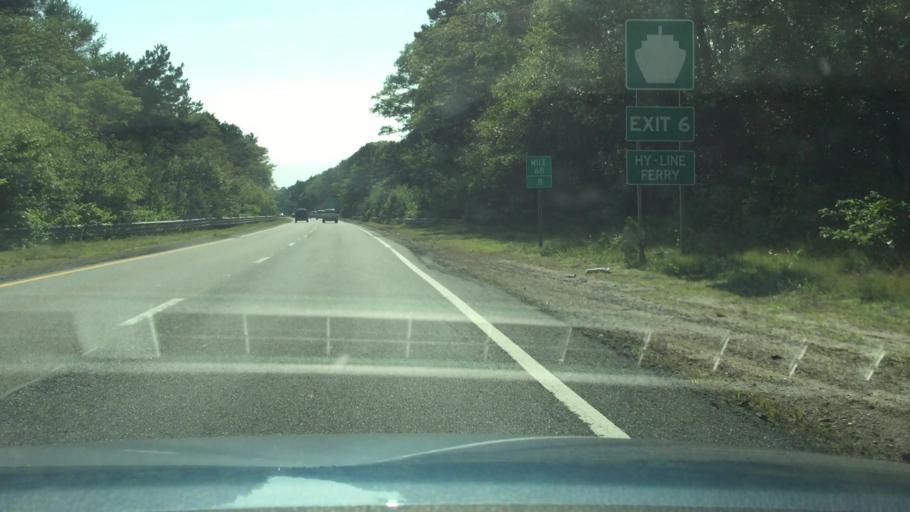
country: US
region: Massachusetts
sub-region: Barnstable County
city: Barnstable
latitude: 41.6905
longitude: -70.3250
